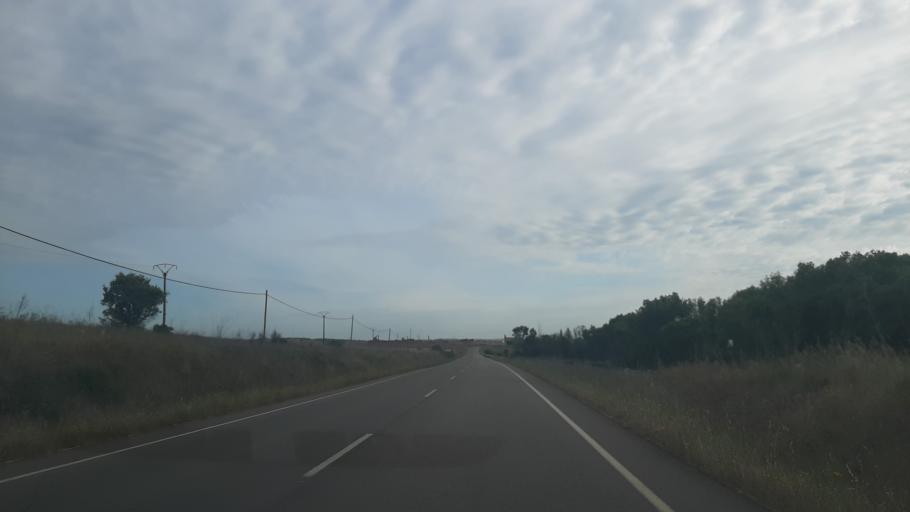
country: ES
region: Castille and Leon
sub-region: Provincia de Salamanca
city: Gallegos de Arganan
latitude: 40.6148
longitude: -6.7061
